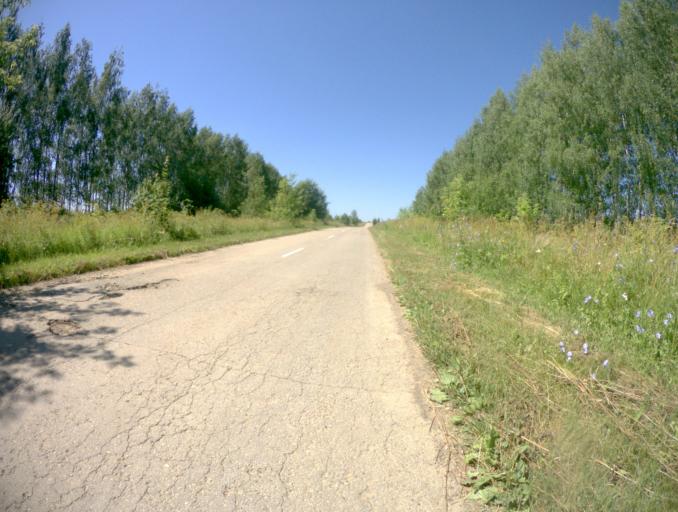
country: RU
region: Nizjnij Novgorod
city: Reshetikha
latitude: 56.1146
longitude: 43.2380
